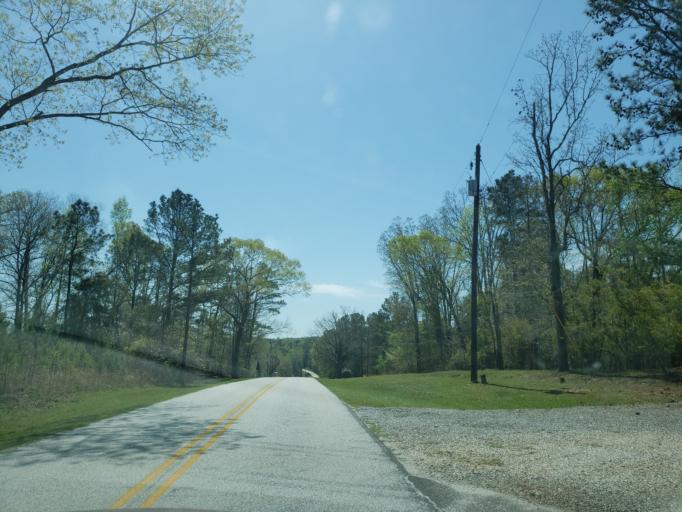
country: US
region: Alabama
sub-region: Elmore County
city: Tallassee
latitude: 32.6778
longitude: -85.8631
